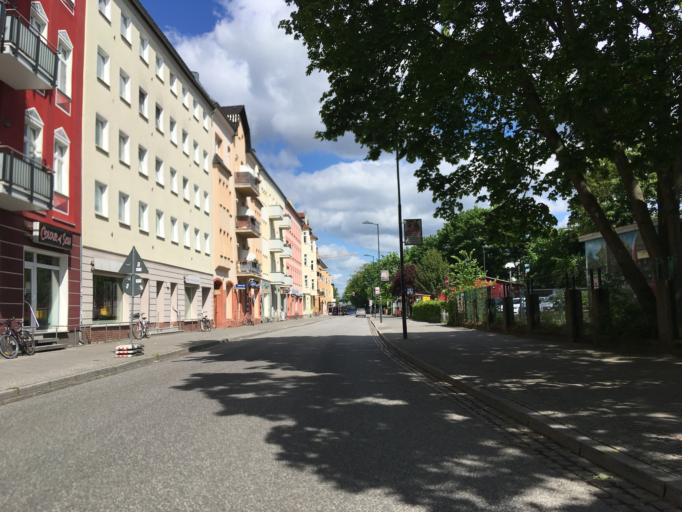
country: DE
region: Brandenburg
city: Oranienburg
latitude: 52.7553
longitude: 13.2474
